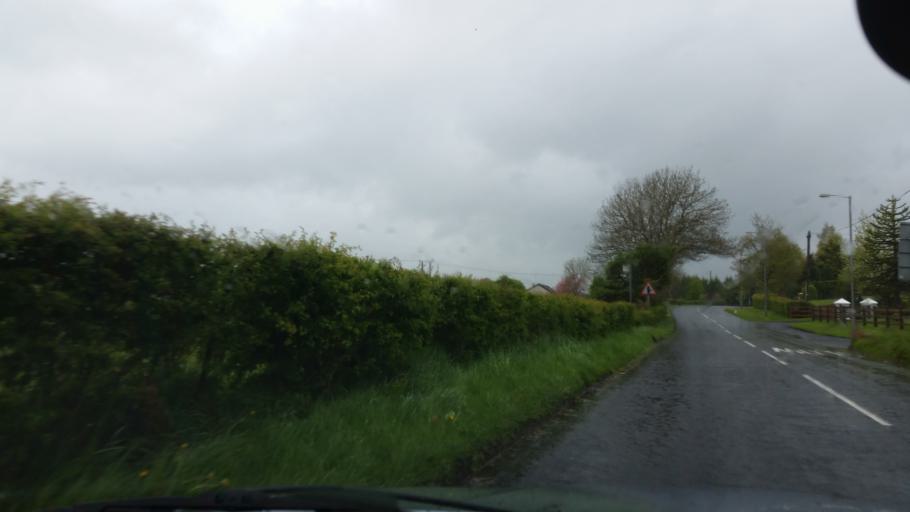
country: GB
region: Northern Ireland
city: Fintona
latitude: 54.5297
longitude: -7.2945
